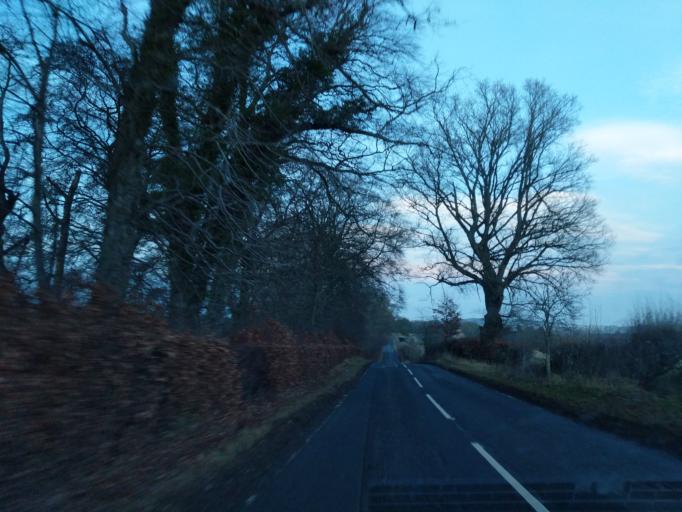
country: GB
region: Scotland
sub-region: Midlothian
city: Bonnyrigg
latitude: 55.8130
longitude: -3.1049
